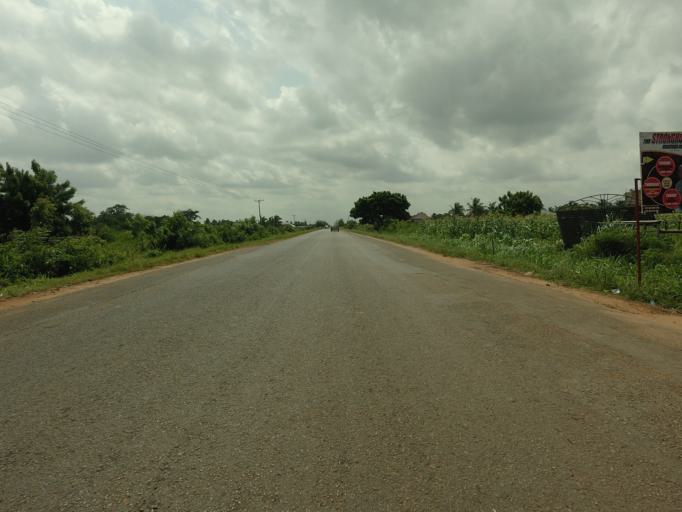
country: TG
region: Maritime
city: Lome
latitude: 6.1315
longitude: 1.1206
